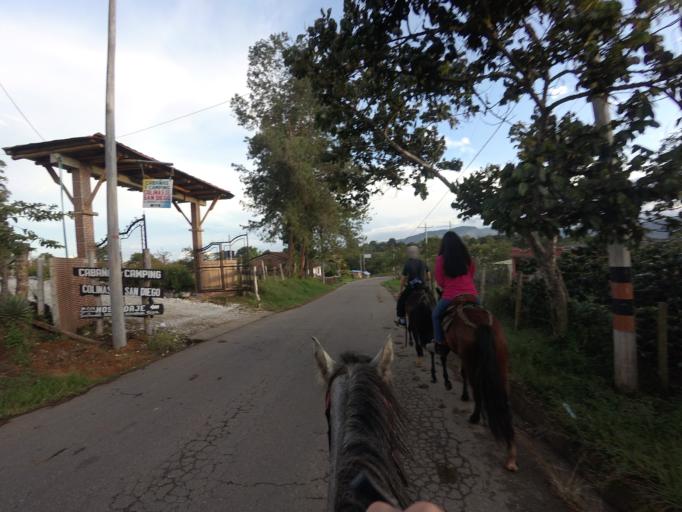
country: CO
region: Huila
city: San Agustin
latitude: 1.8948
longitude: -76.2731
